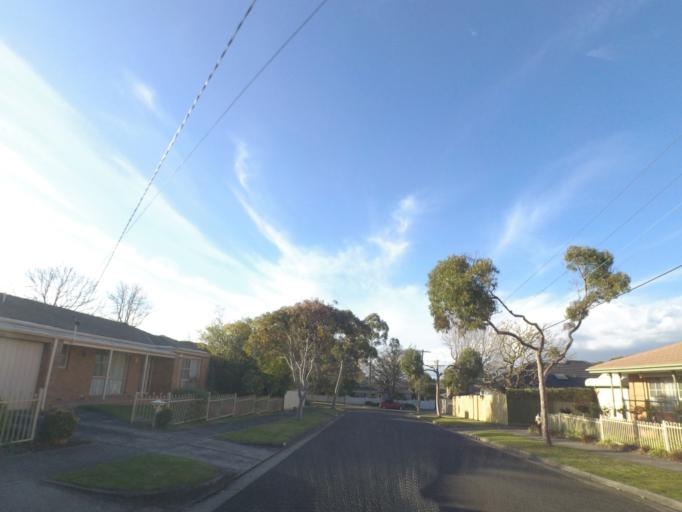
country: AU
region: Victoria
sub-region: Whitehorse
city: Blackburn North
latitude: -37.8089
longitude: 145.1546
